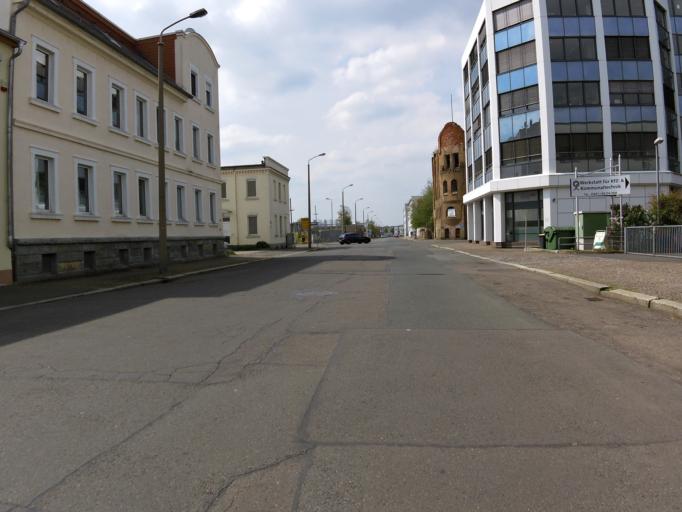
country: DE
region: Saxony
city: Leipzig
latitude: 51.3584
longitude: 12.3921
